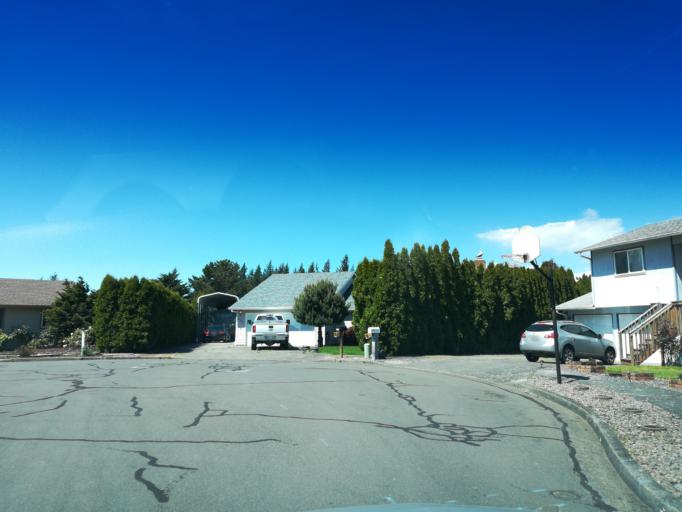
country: US
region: Oregon
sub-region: Multnomah County
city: Troutdale
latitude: 45.5253
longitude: -122.3777
